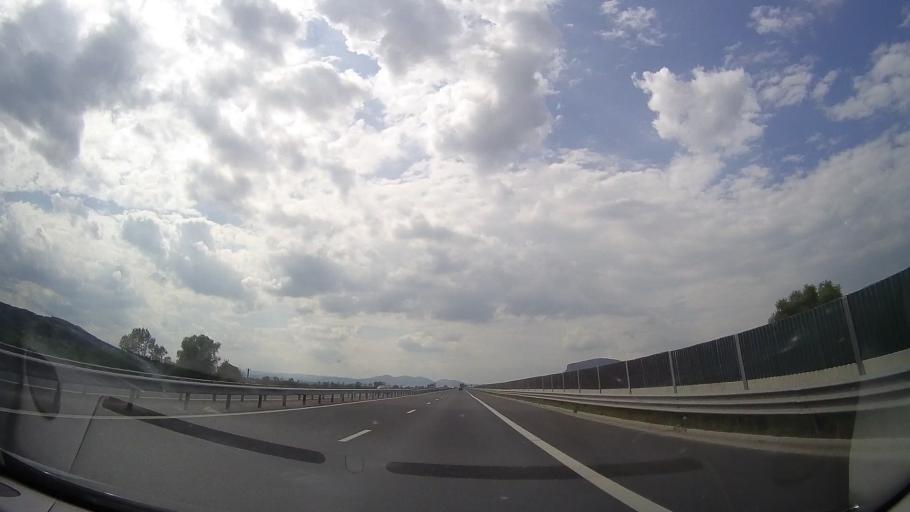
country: RO
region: Hunedoara
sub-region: Comuna Rapoltu Mare
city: Rapoltu Mare
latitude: 45.8411
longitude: 23.0839
